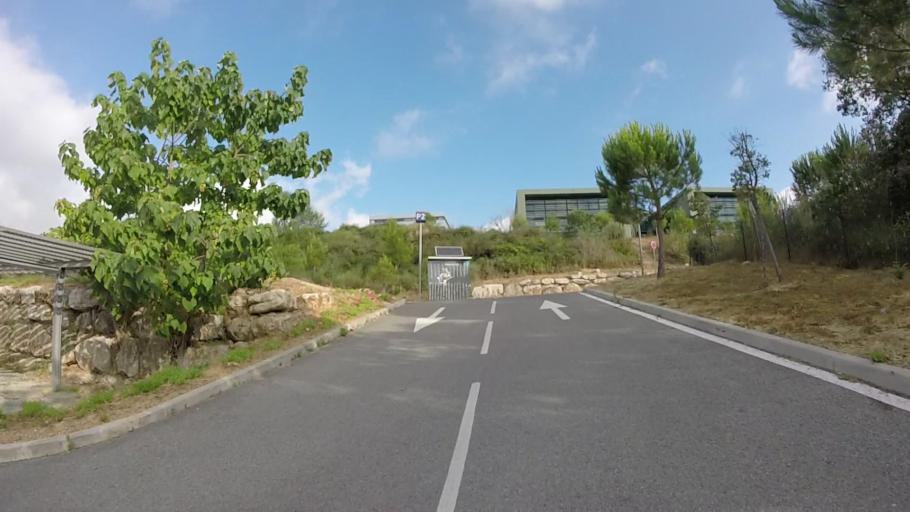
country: FR
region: Provence-Alpes-Cote d'Azur
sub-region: Departement des Alpes-Maritimes
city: Biot
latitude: 43.6147
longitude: 7.0732
